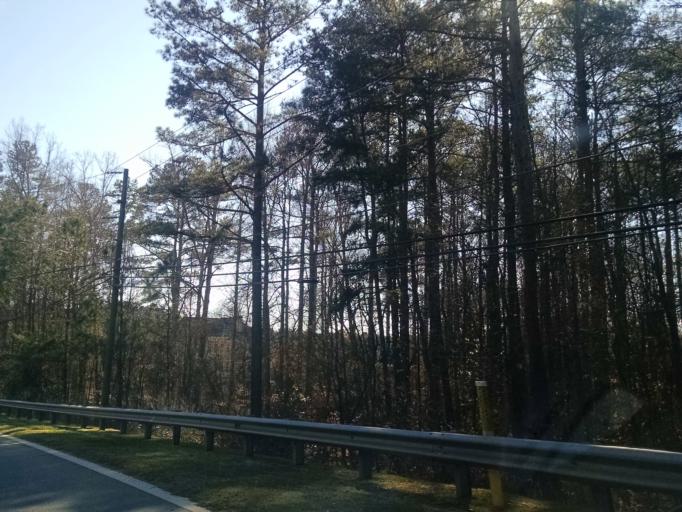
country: US
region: Georgia
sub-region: Gwinnett County
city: Suwanee
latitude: 34.0805
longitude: -84.0736
